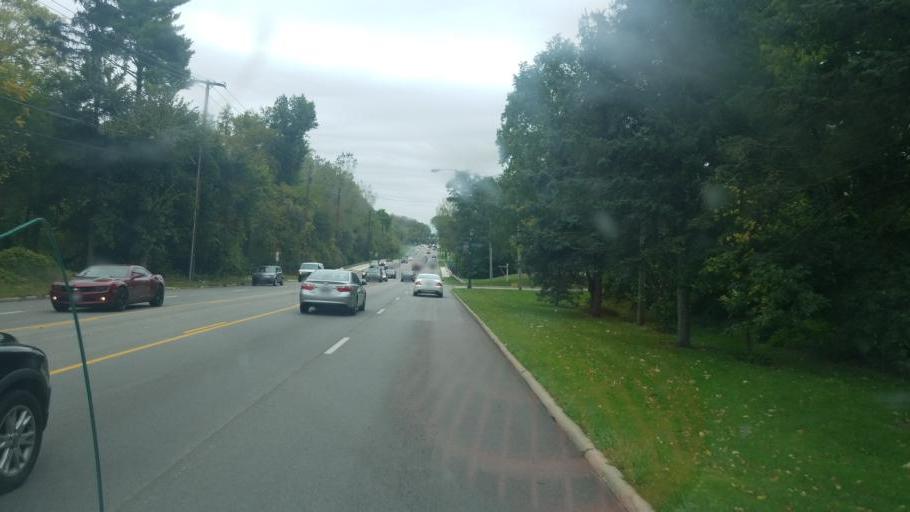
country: US
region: Ohio
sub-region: Lucas County
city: Ottawa Hills
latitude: 41.6768
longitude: -83.6620
